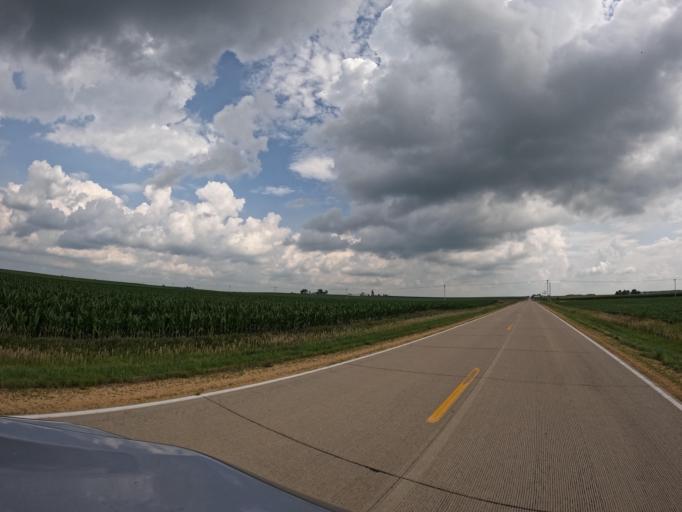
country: US
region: Iowa
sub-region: Clinton County
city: De Witt
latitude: 41.7879
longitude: -90.4132
